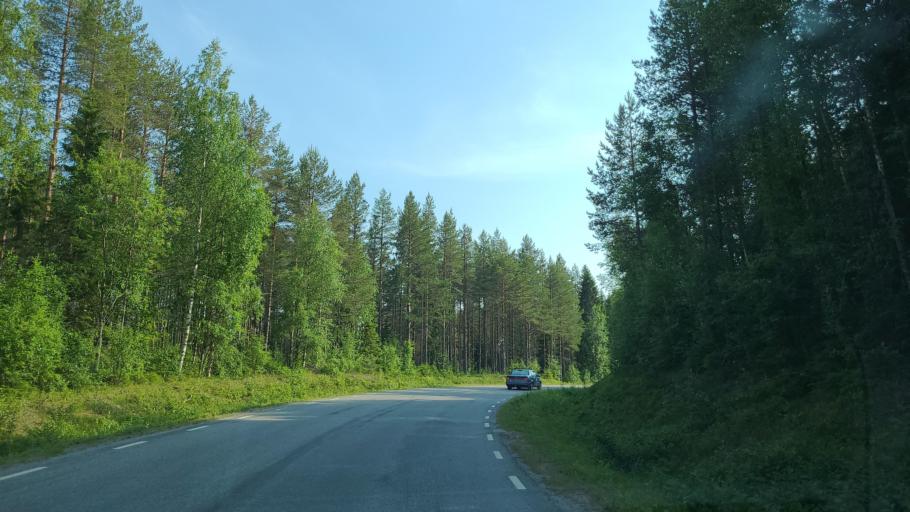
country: SE
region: Vaesterbotten
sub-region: Skelleftea Kommun
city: Burea
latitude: 64.3552
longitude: 21.3380
